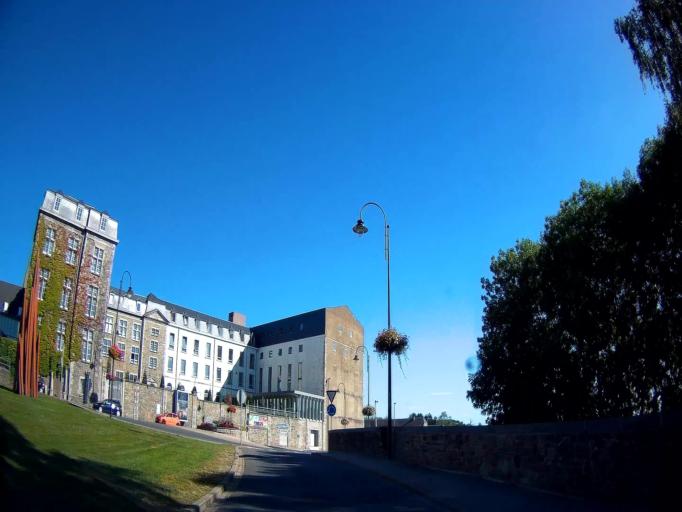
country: BE
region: Wallonia
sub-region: Province du Luxembourg
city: Bastogne
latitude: 50.0051
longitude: 5.7224
